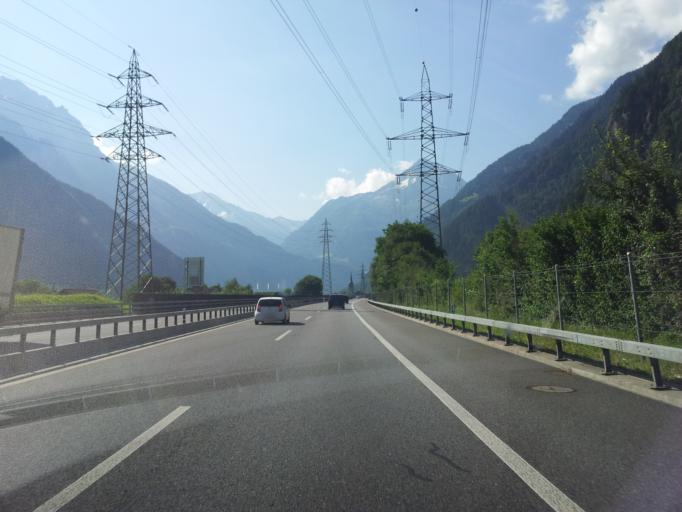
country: CH
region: Uri
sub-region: Uri
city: Erstfeld
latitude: 46.8305
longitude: 8.6386
